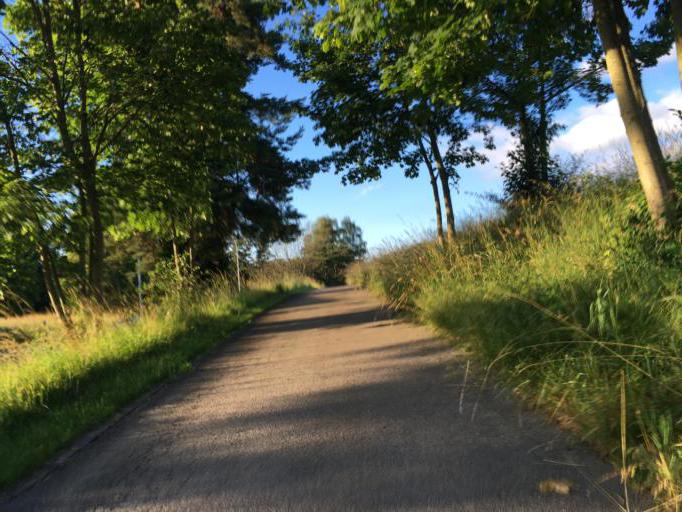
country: CH
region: Zurich
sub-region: Bezirk Meilen
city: Zollikon
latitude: 47.3419
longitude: 8.5823
